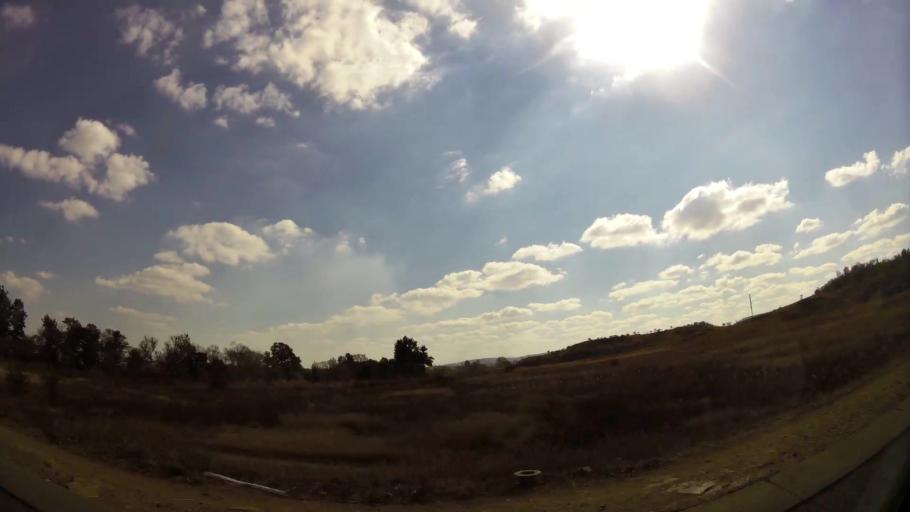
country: ZA
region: Gauteng
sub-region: City of Tshwane Metropolitan Municipality
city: Cullinan
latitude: -25.7445
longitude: 28.3735
